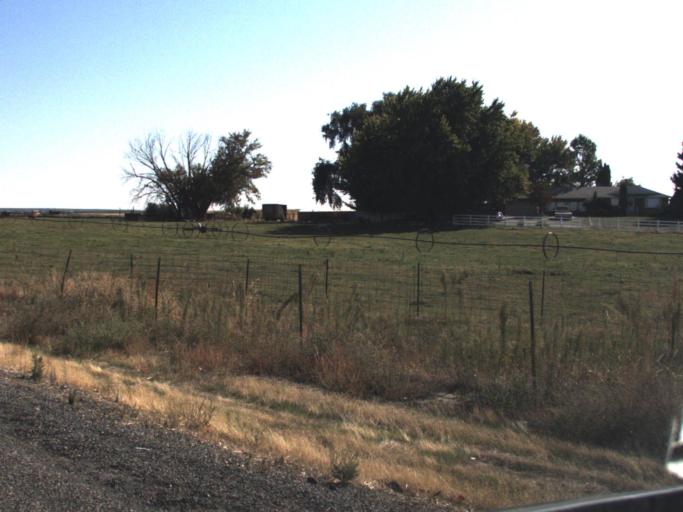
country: US
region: Washington
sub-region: Walla Walla County
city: Burbank
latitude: 46.2118
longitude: -118.9502
